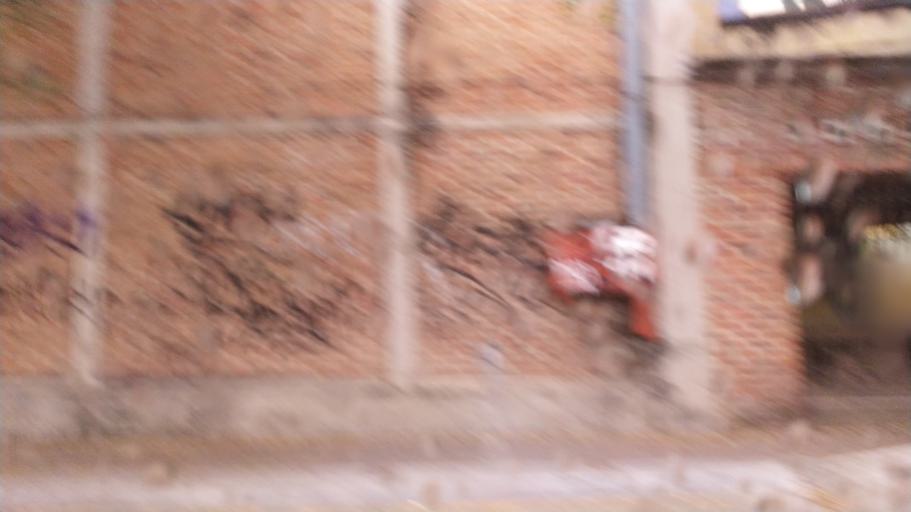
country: MX
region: Jalisco
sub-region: Zapopan
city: Zapopan
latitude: 20.7198
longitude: -103.3677
